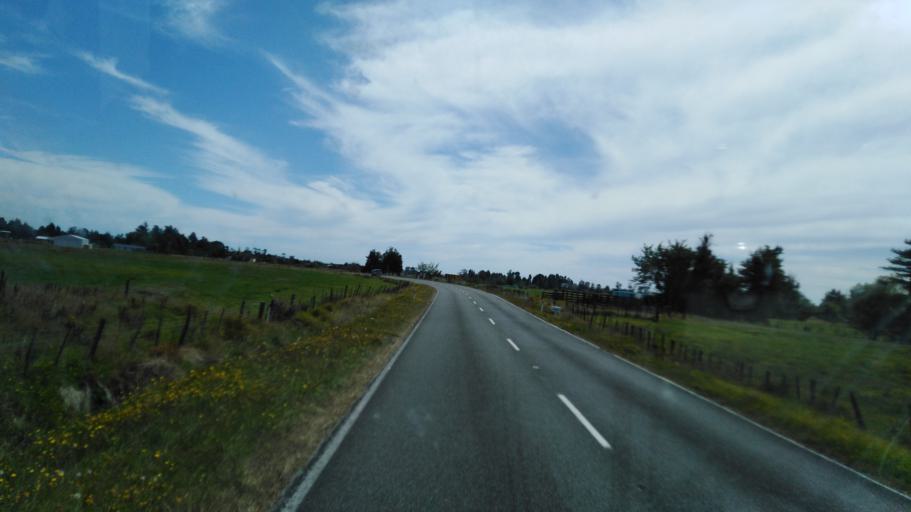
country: NZ
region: West Coast
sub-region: Buller District
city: Westport
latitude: -41.7575
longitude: 171.6407
